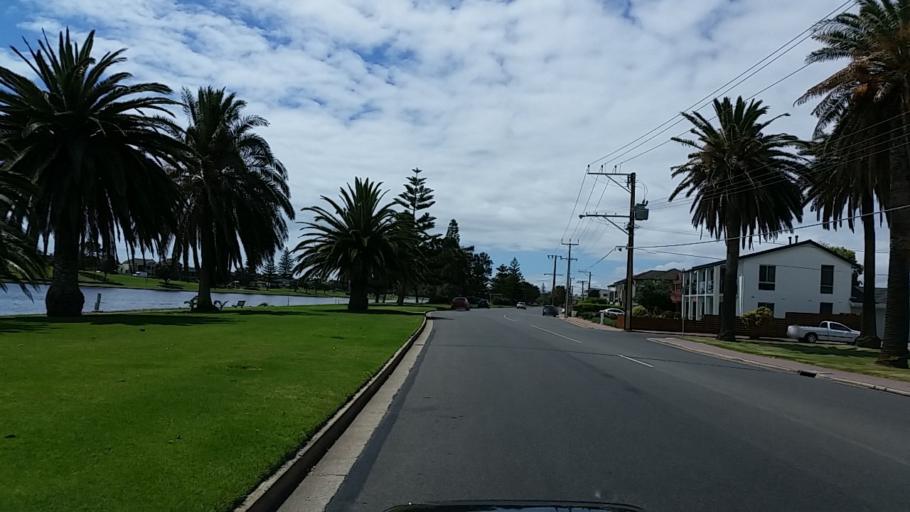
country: AU
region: South Australia
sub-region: Adelaide
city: Glenelg
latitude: -34.9708
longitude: 138.5141
